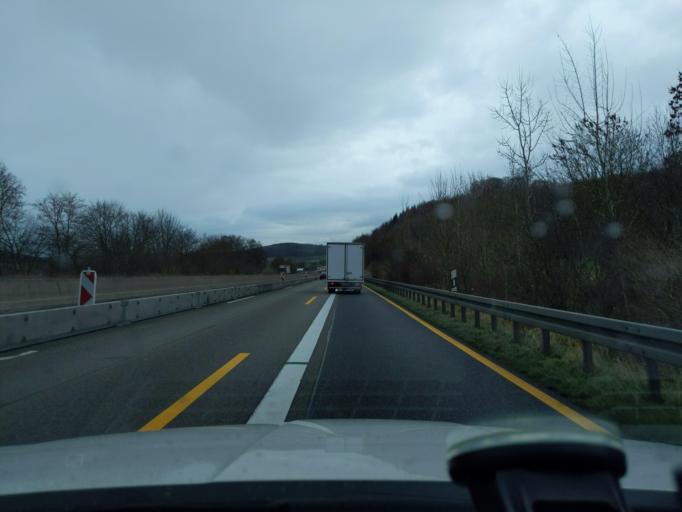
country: DE
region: North Rhine-Westphalia
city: Warburg
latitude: 51.4773
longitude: 9.0627
